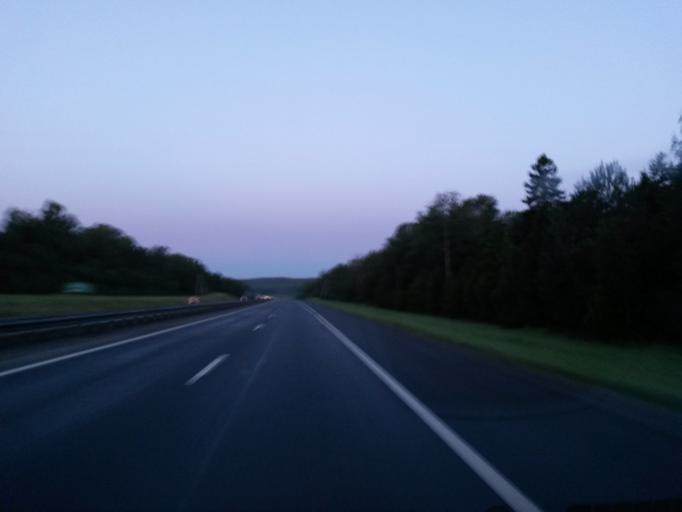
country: RU
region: Vladimir
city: Arsaki
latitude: 56.4902
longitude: 38.4347
